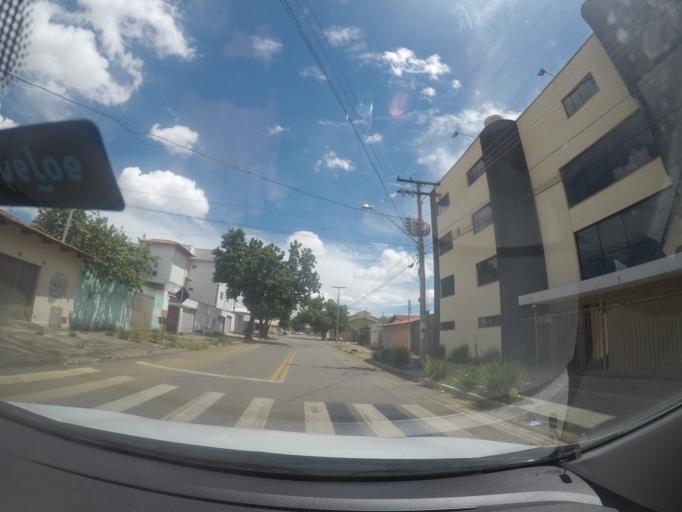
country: BR
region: Goias
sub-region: Goiania
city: Goiania
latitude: -16.6785
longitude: -49.3170
